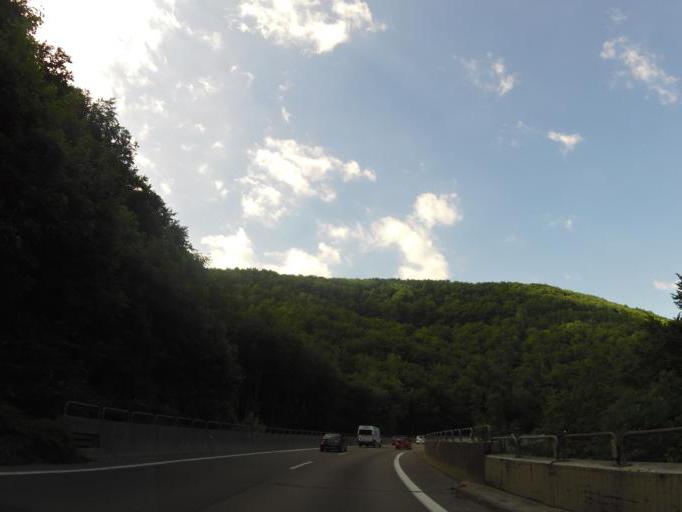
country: DE
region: Baden-Wuerttemberg
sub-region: Regierungsbezirk Stuttgart
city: Muhlhausen
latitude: 48.5676
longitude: 9.6466
